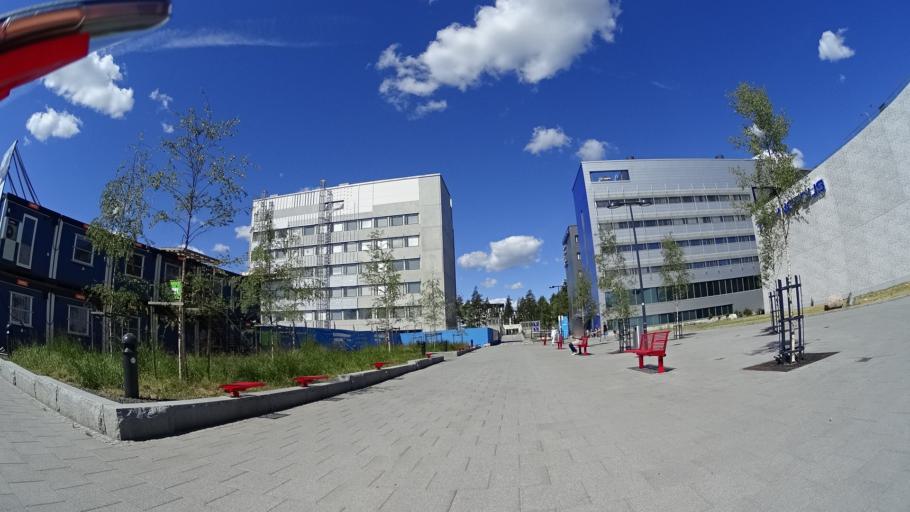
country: FI
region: Uusimaa
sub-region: Helsinki
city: Vantaa
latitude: 60.3045
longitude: 24.9665
